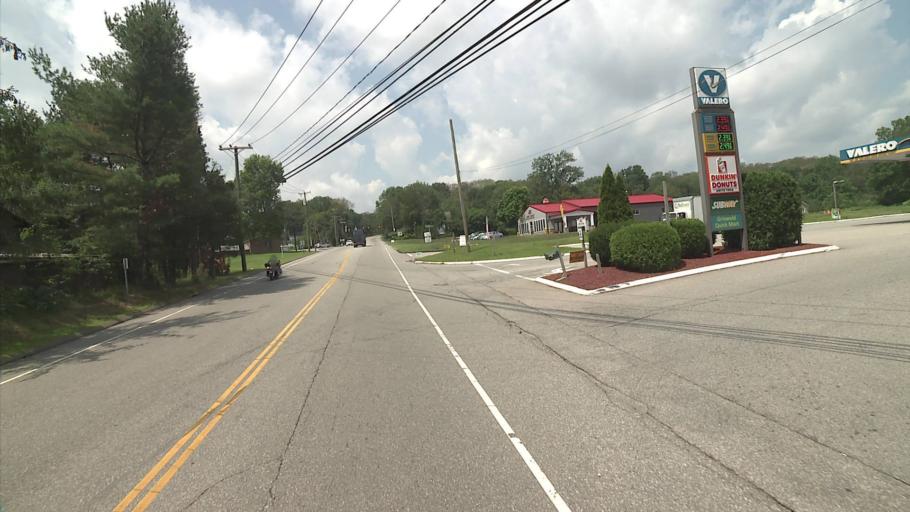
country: US
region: Connecticut
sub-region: New London County
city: Jewett City
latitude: 41.5847
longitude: -71.9392
